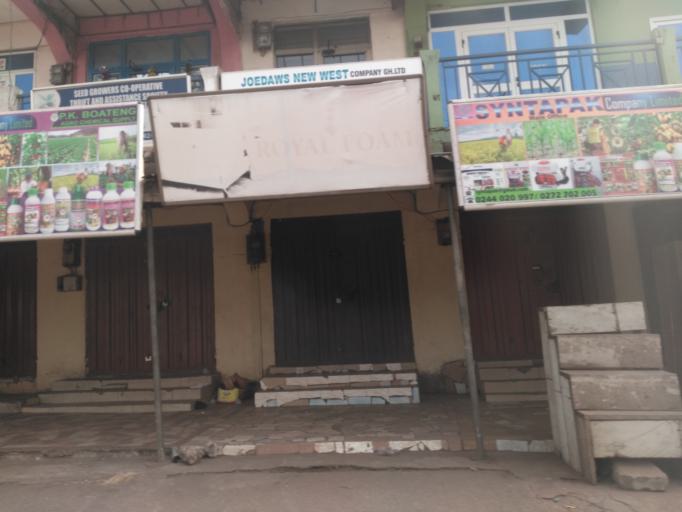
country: GH
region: Ashanti
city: Kumasi
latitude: 6.7062
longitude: -1.6236
